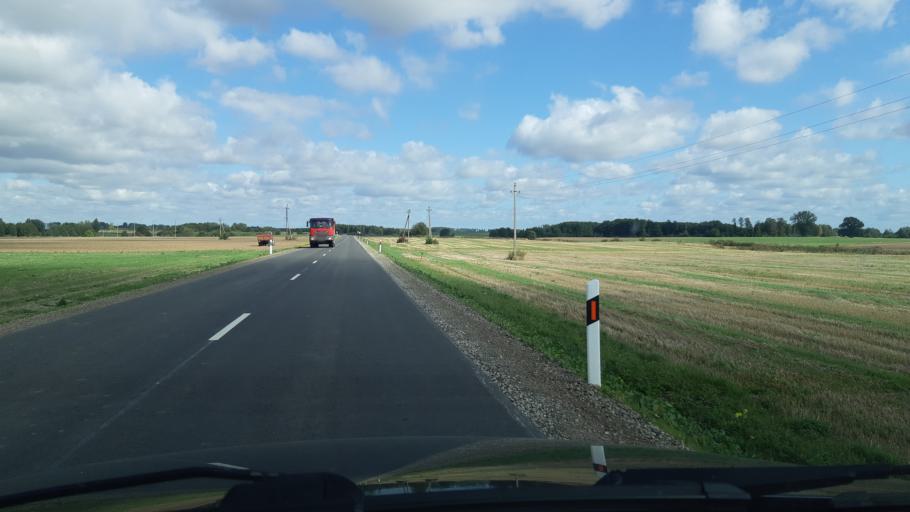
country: LT
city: Virbalis
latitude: 54.6368
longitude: 22.8336
